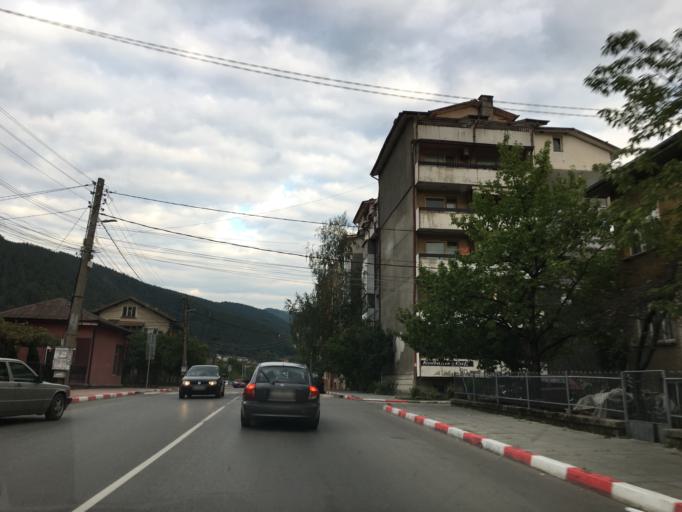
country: BG
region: Sofiya
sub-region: Obshtina Svoge
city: Svoge
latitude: 42.9621
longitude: 23.3451
